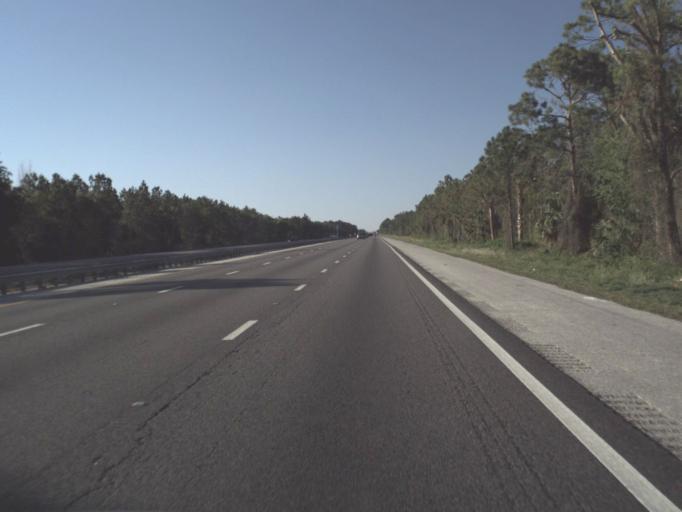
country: US
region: Florida
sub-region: Flagler County
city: Flagler Beach
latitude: 29.4501
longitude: -81.1738
